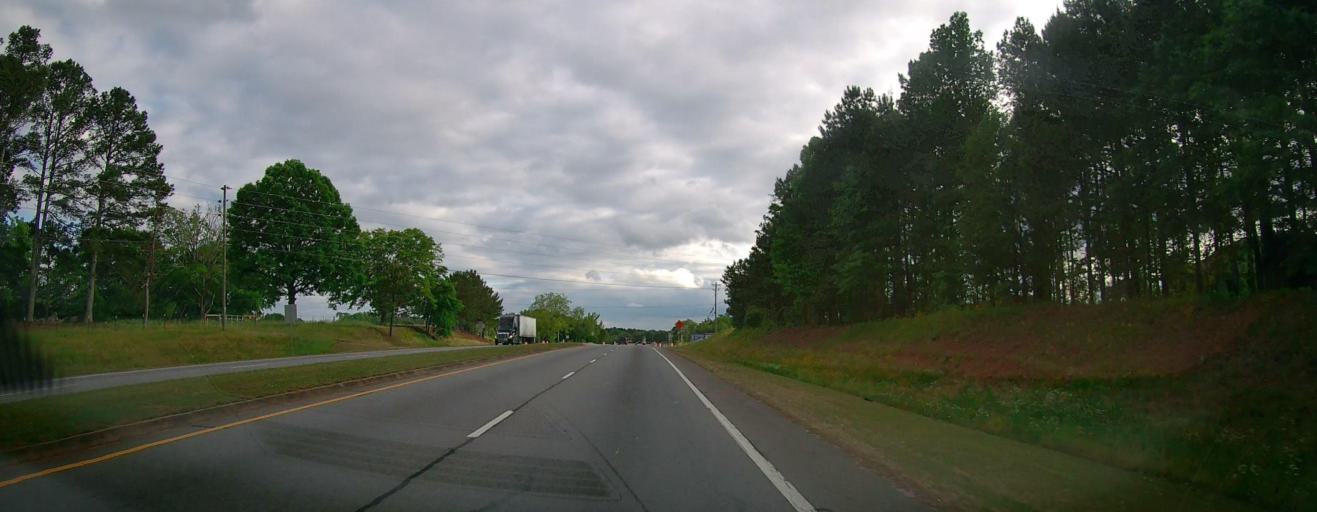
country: US
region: Georgia
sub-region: Oconee County
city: Watkinsville
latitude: 33.8950
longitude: -83.4107
